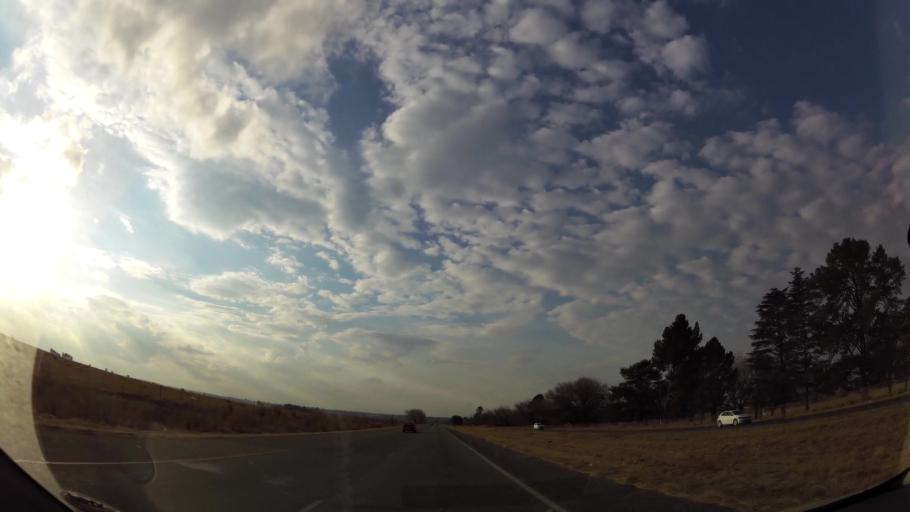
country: ZA
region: Orange Free State
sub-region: Fezile Dabi District Municipality
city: Sasolburg
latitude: -26.7734
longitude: 27.8248
